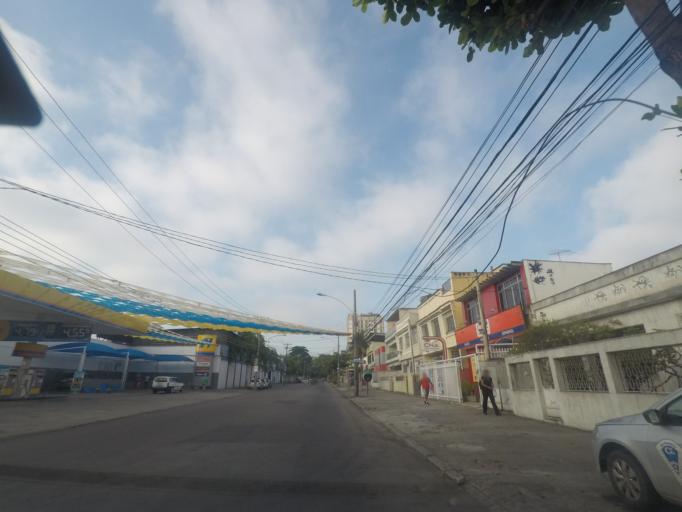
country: BR
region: Rio de Janeiro
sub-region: Duque De Caxias
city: Duque de Caxias
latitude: -22.8403
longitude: -43.2669
